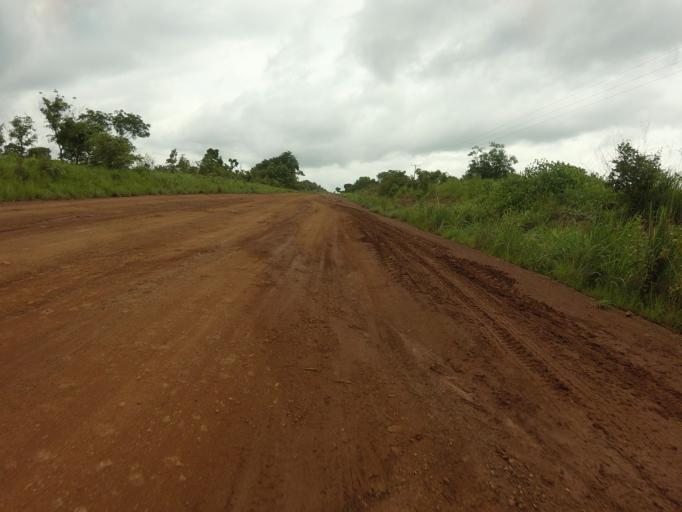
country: GH
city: Kpandae
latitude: 8.3152
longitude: 0.4792
